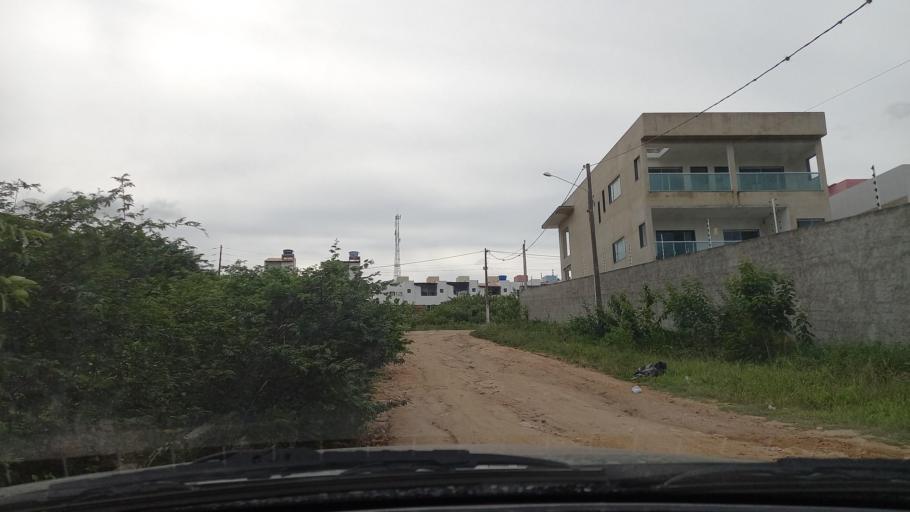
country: BR
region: Pernambuco
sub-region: Gravata
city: Gravata
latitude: -8.2227
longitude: -35.5761
